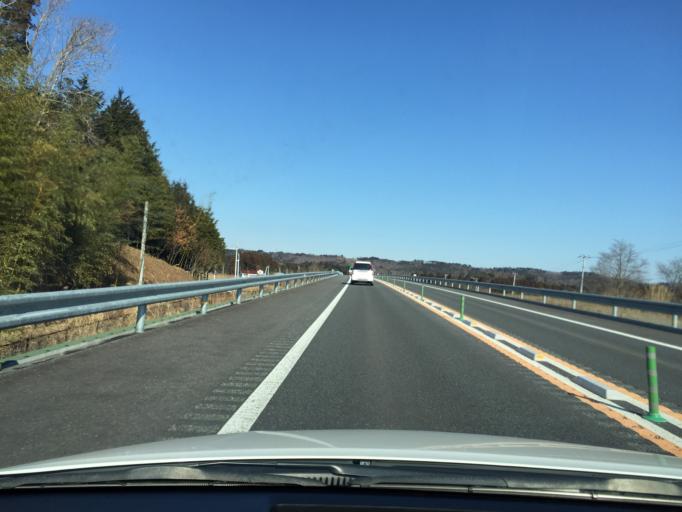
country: JP
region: Fukushima
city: Namie
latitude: 37.5652
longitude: 140.9449
